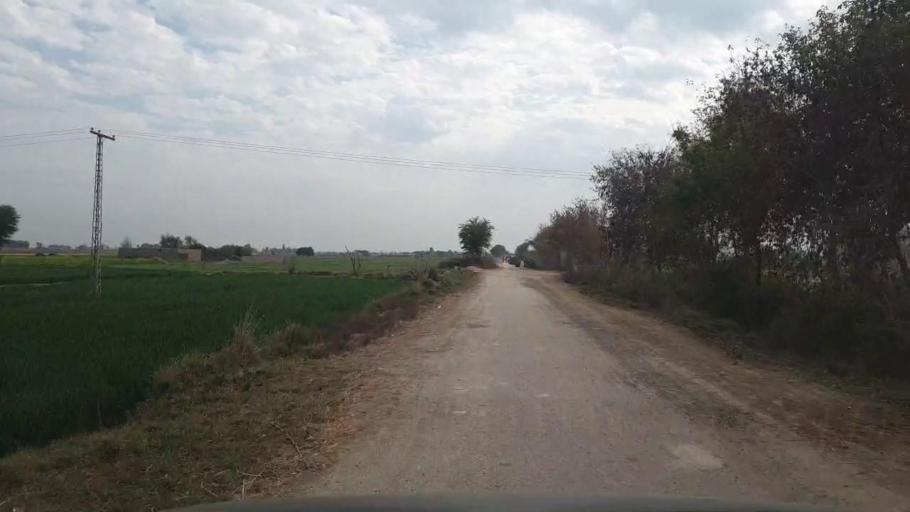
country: PK
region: Sindh
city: Sakrand
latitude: 26.0145
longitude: 68.4313
